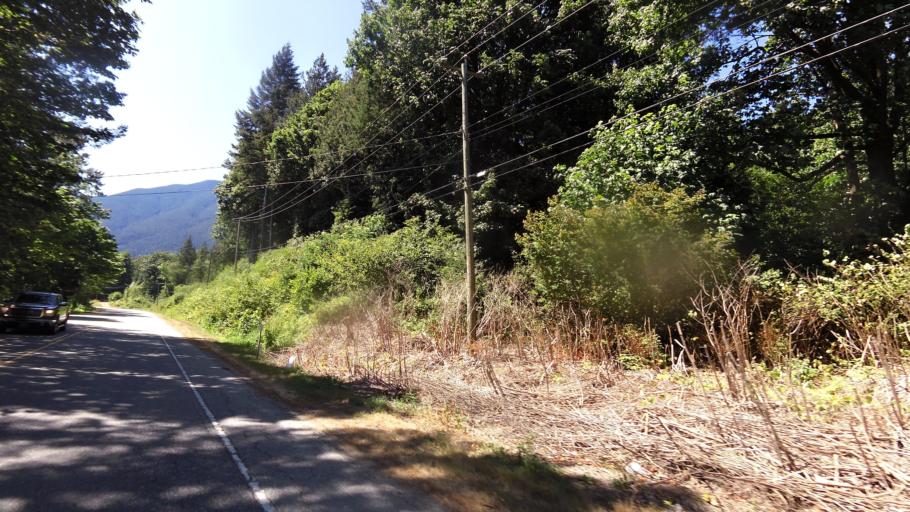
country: CA
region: British Columbia
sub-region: Fraser Valley Regional District
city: Chilliwack
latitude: 49.2437
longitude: -121.9921
